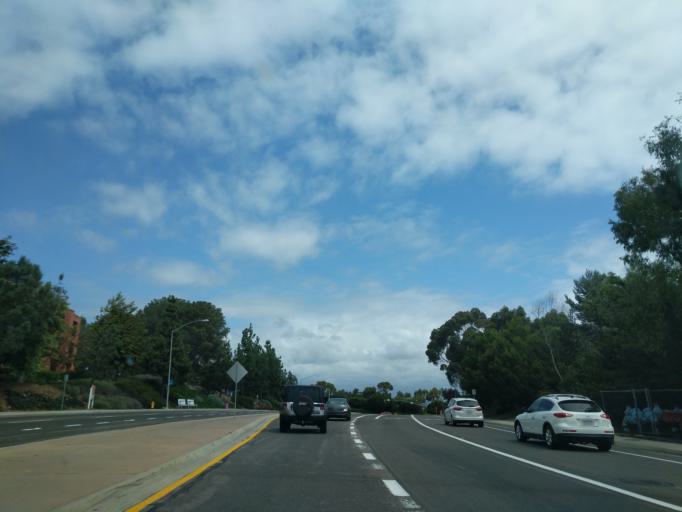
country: US
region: California
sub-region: San Diego County
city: La Jolla
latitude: 32.8907
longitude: -117.2418
